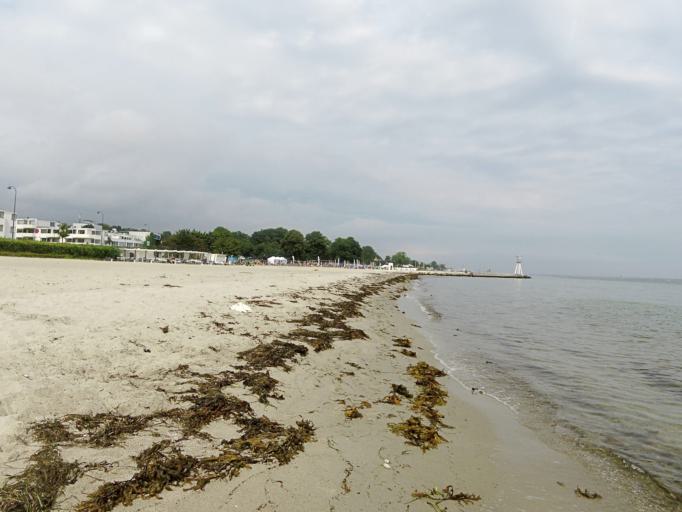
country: DK
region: Capital Region
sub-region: Gentofte Kommune
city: Charlottenlund
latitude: 55.7753
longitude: 12.5923
